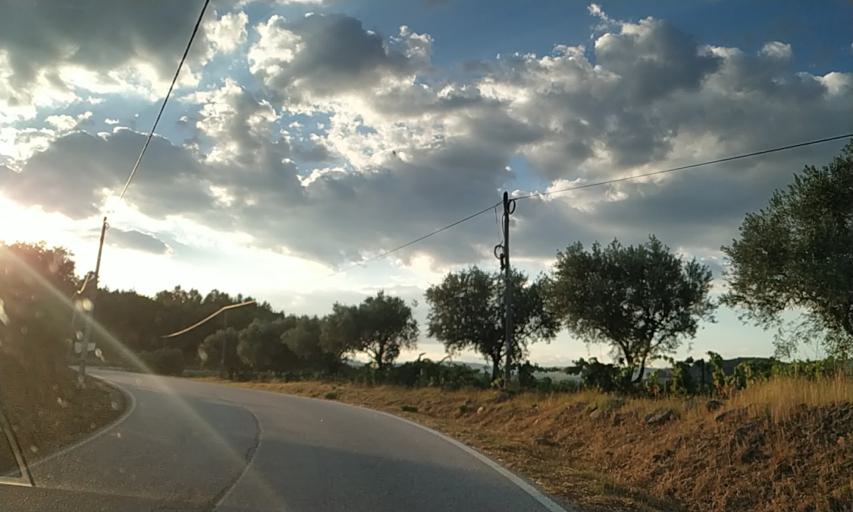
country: PT
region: Viseu
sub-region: Sao Joao da Pesqueira
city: Sao Joao da Pesqueira
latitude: 41.2604
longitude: -7.4426
